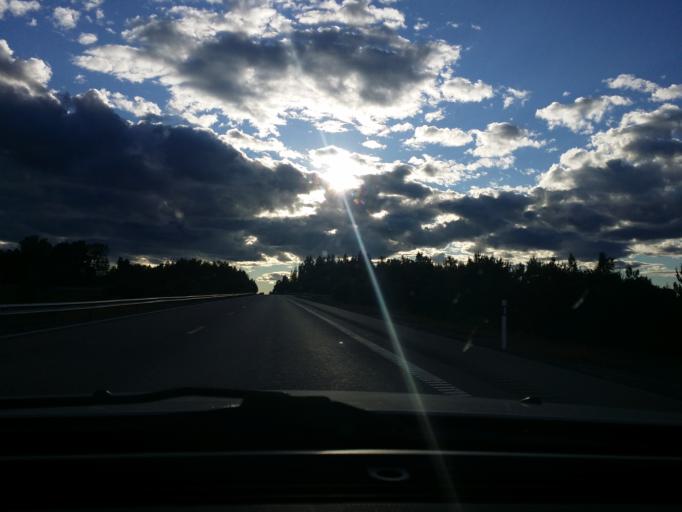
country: SE
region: Uppsala
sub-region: Enkopings Kommun
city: Grillby
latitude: 59.6364
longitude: 17.2746
